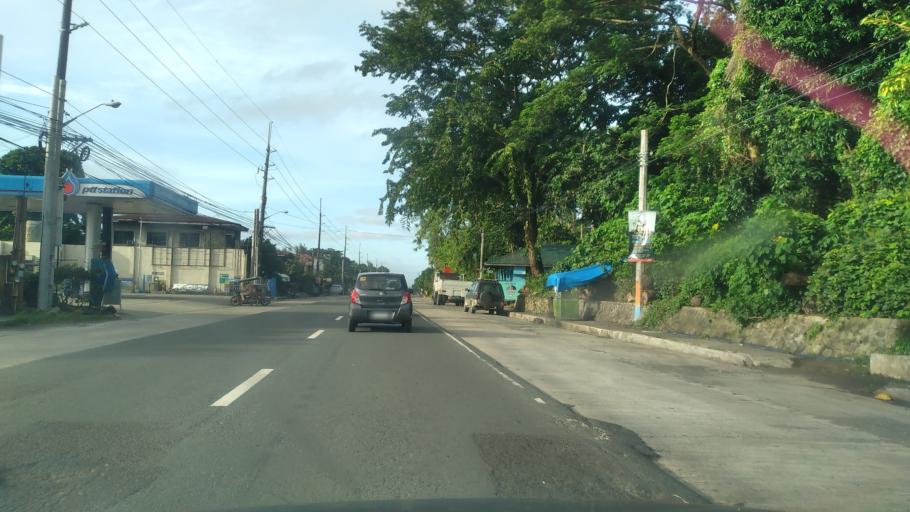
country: PH
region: Calabarzon
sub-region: Province of Quezon
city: Calumpang
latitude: 13.9735
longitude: 121.5544
